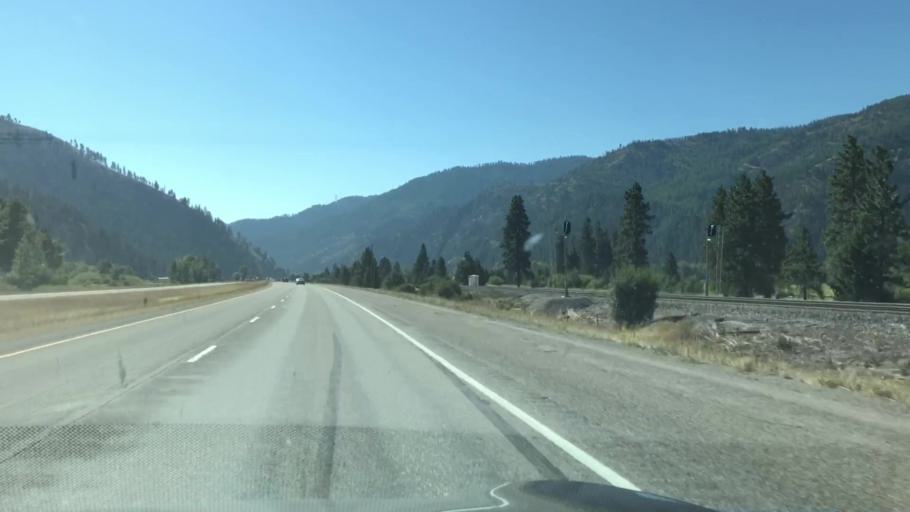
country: US
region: Montana
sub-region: Missoula County
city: Clinton
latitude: 46.7496
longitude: -113.7060
